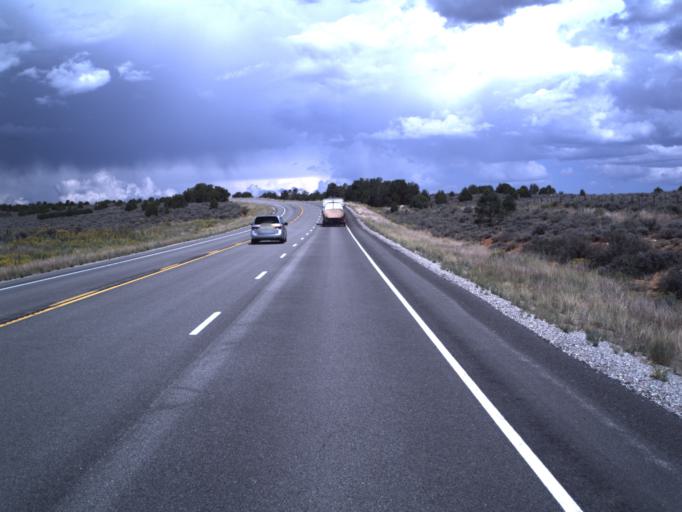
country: US
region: Utah
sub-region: San Juan County
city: Blanding
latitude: 37.7044
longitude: -109.4243
